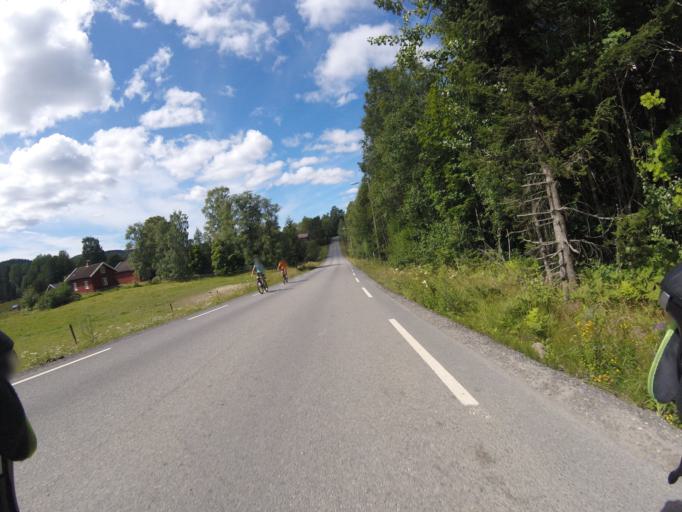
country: NO
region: Akershus
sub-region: Lorenskog
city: Kjenn
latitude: 59.8957
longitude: 10.9728
